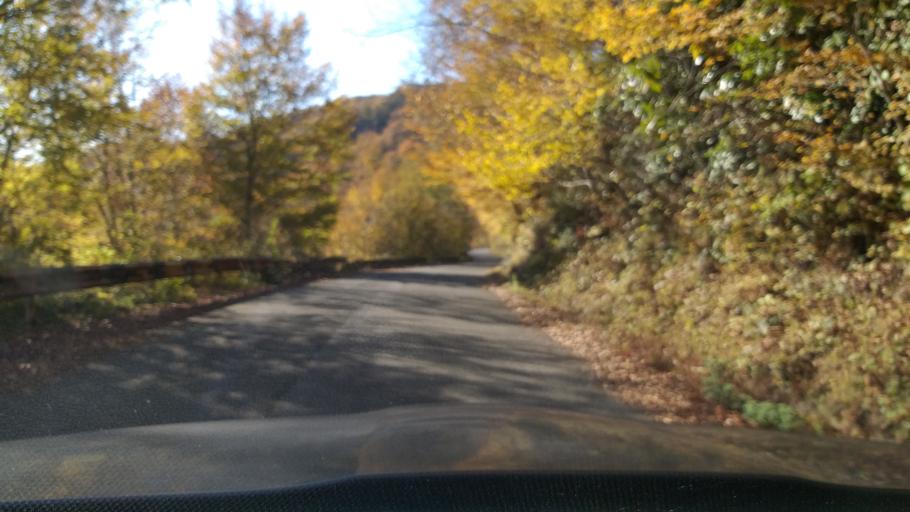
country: GE
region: Abkhazia
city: Bich'vinta
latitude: 43.1915
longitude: 40.4551
